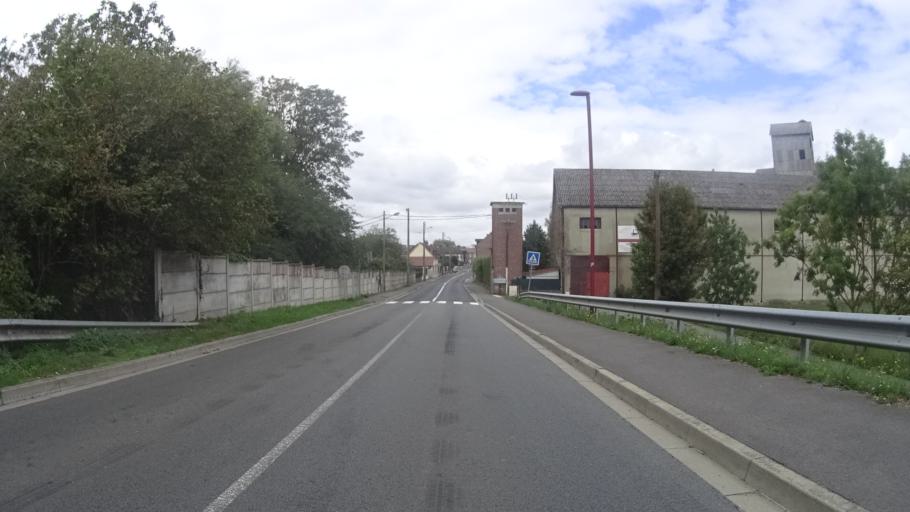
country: FR
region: Picardie
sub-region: Departement de l'Oise
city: Noyon
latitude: 49.5623
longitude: 2.9910
